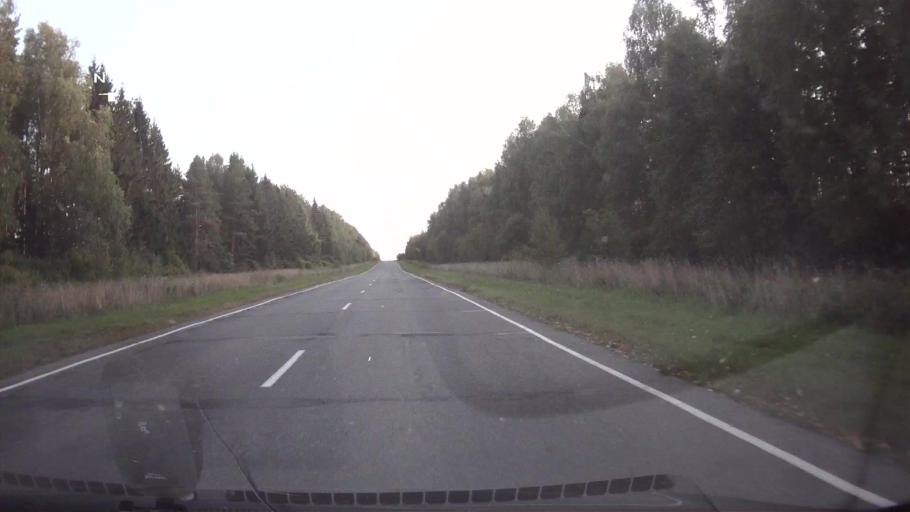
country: RU
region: Mariy-El
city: Kuzhener
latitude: 56.8774
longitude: 48.7538
